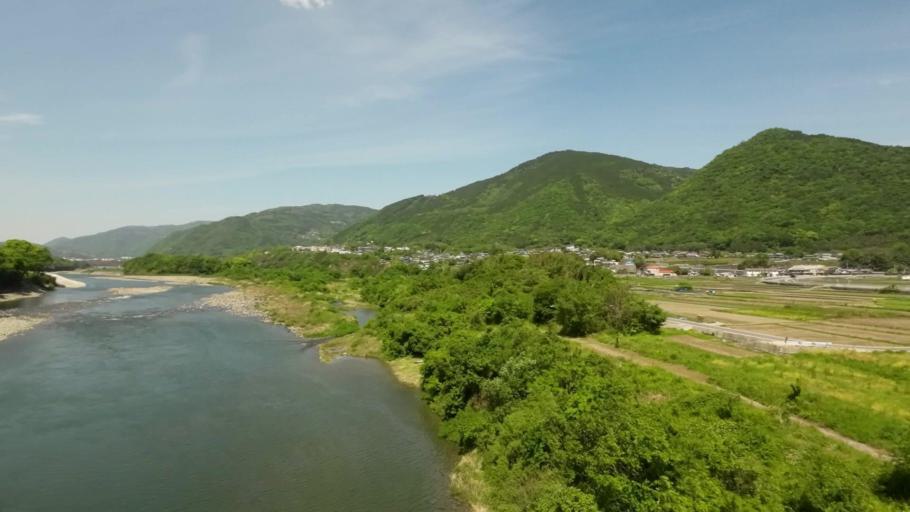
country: JP
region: Tokushima
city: Ikedacho
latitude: 34.0364
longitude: 133.8642
